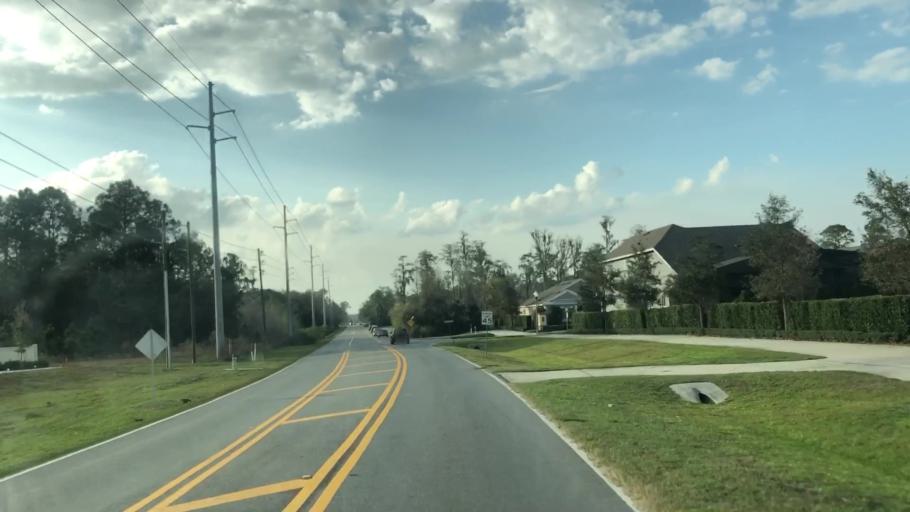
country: US
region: Florida
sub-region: Orange County
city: Bay Hill
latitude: 28.4347
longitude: -81.5819
